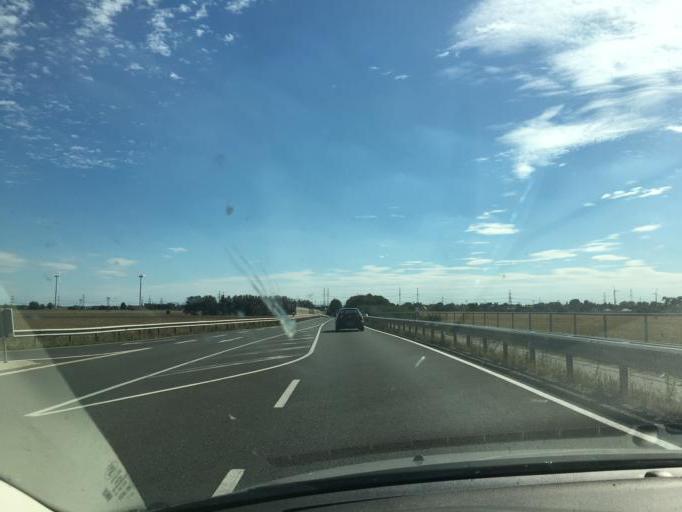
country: DE
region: Saxony-Anhalt
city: Colbitz
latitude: 52.2872
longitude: 11.6235
